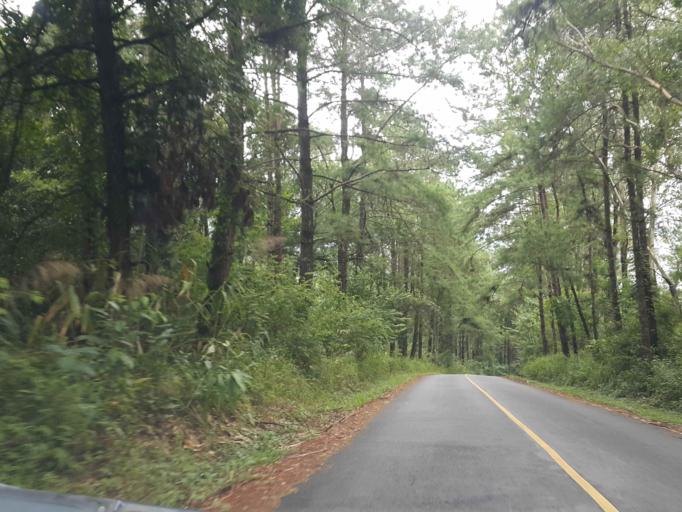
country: TH
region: Chiang Mai
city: Mae Chaem
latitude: 18.5183
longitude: 98.4796
